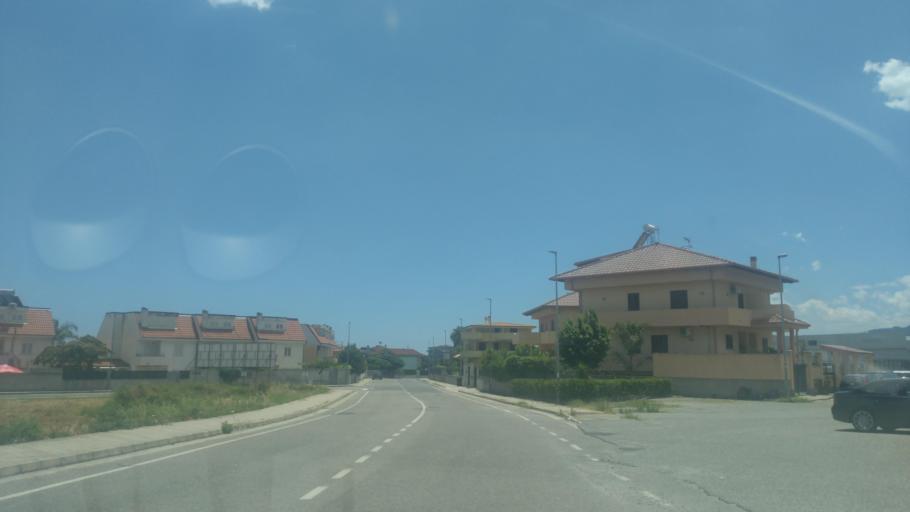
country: IT
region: Calabria
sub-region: Provincia di Catanzaro
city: Montepaone Lido
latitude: 38.7249
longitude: 16.5322
